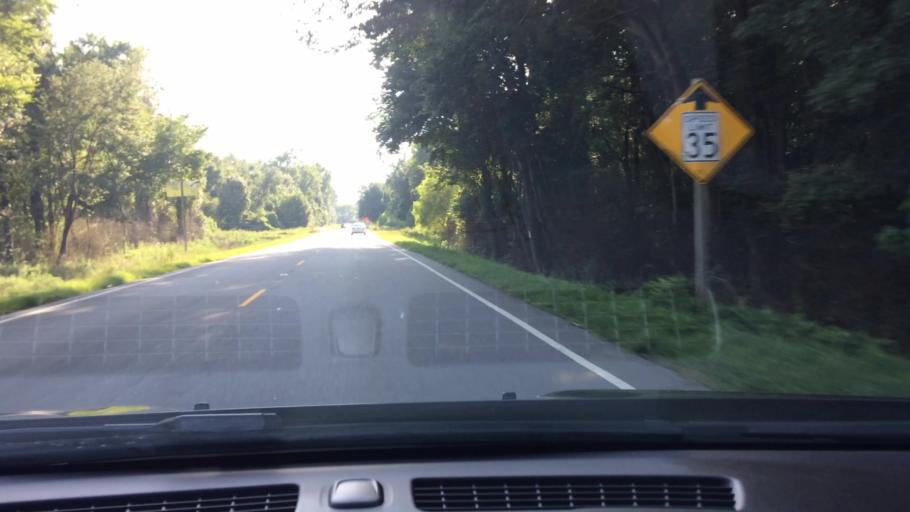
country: US
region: North Carolina
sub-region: Pitt County
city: Ayden
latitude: 35.4715
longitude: -77.3983
